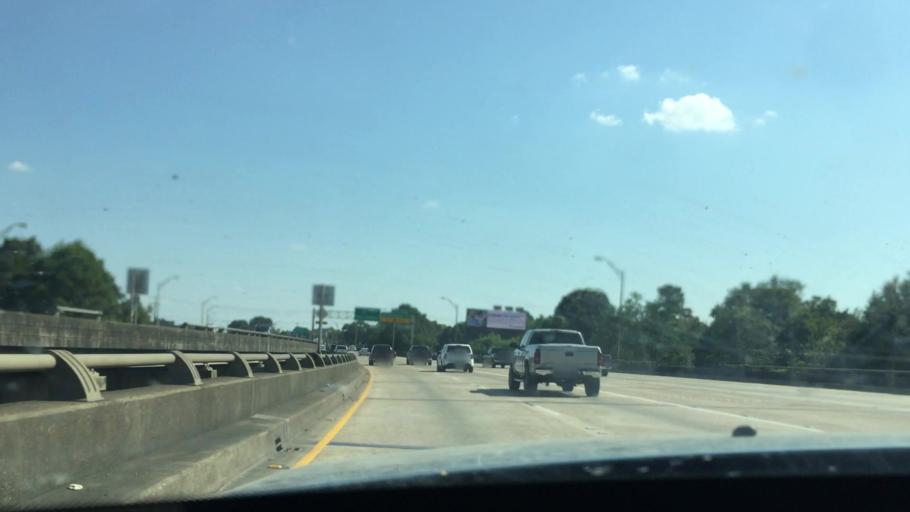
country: US
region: Louisiana
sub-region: East Baton Rouge Parish
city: Baton Rouge
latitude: 30.4363
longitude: -91.1779
